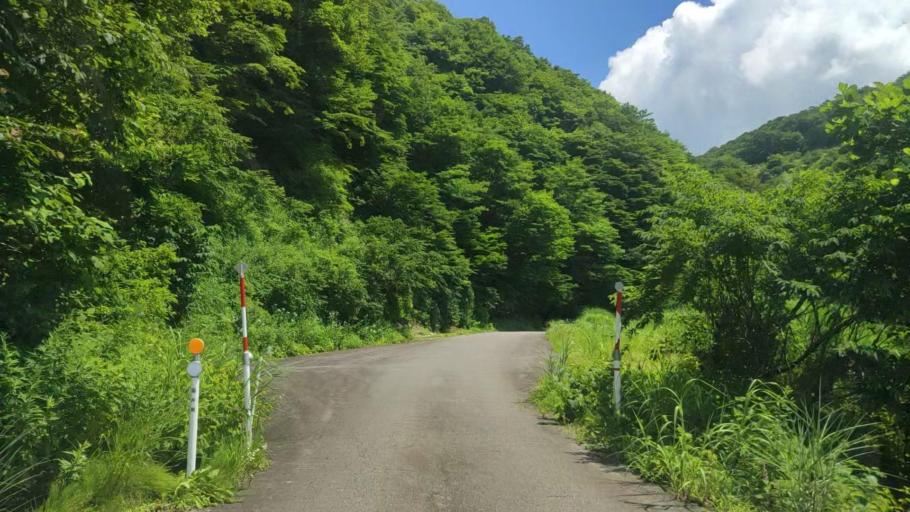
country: JP
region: Fukui
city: Ono
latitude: 35.7831
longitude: 136.5145
